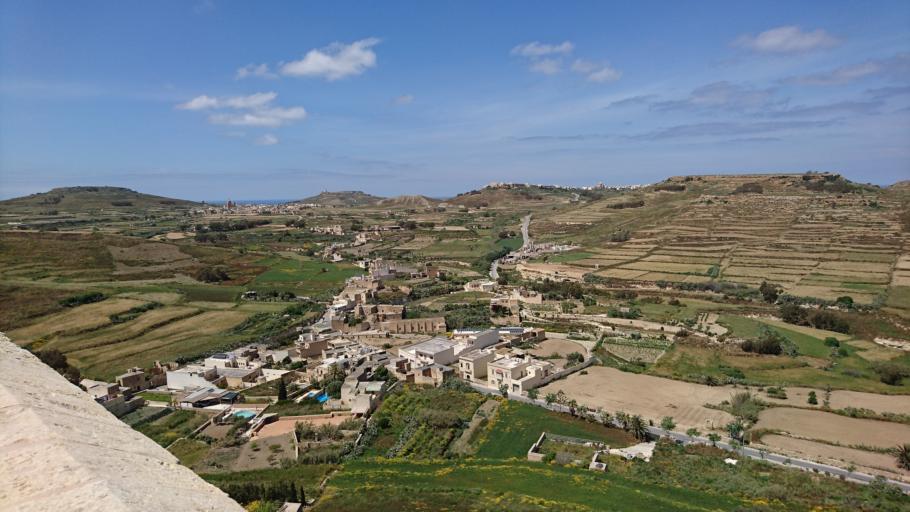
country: MT
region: Victoria
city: Victoria
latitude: 36.0473
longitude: 14.2396
